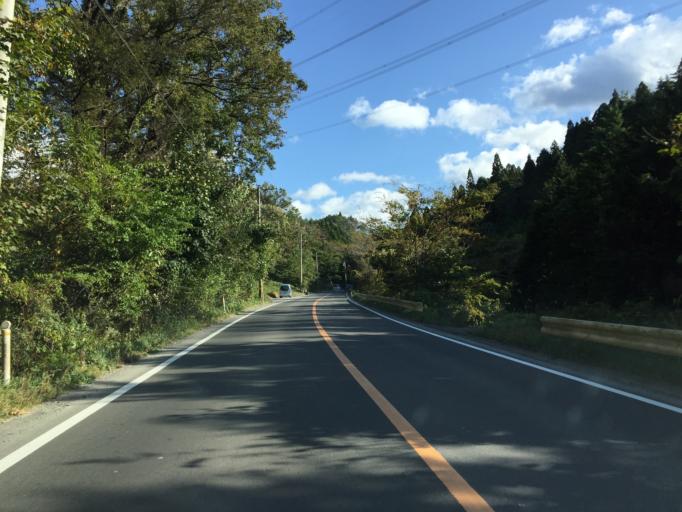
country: JP
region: Miyagi
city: Marumori
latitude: 37.8585
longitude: 140.8475
